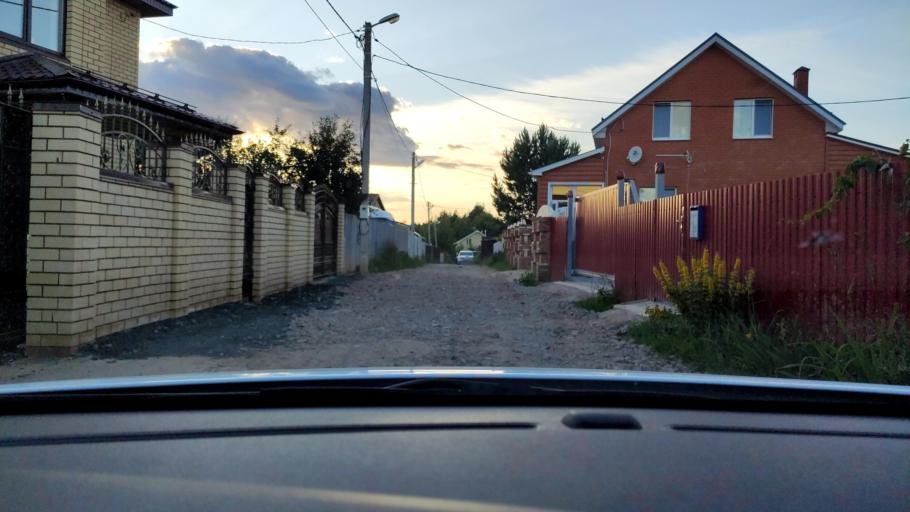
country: RU
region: Tatarstan
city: Stolbishchi
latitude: 55.7605
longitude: 49.3021
